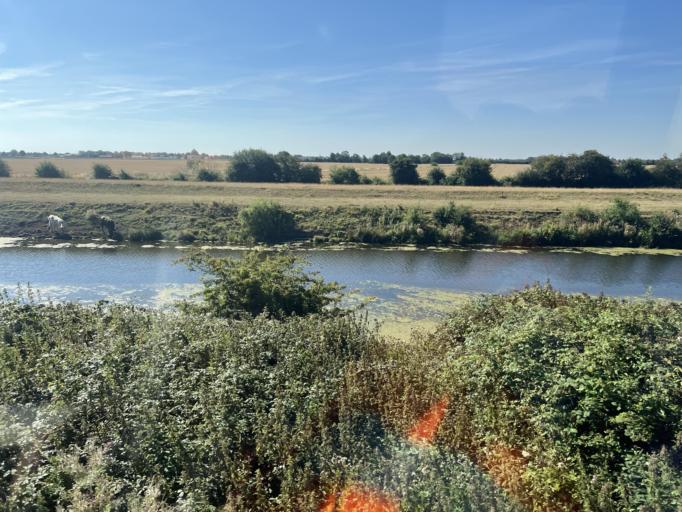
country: GB
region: England
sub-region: Lincolnshire
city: Kirton
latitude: 52.9764
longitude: -0.1336
